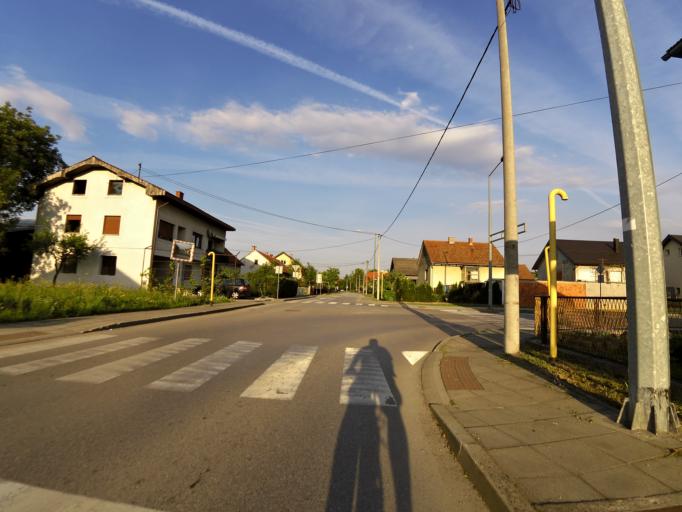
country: HR
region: Karlovacka
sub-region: Grad Karlovac
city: Karlovac
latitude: 45.4971
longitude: 15.5410
